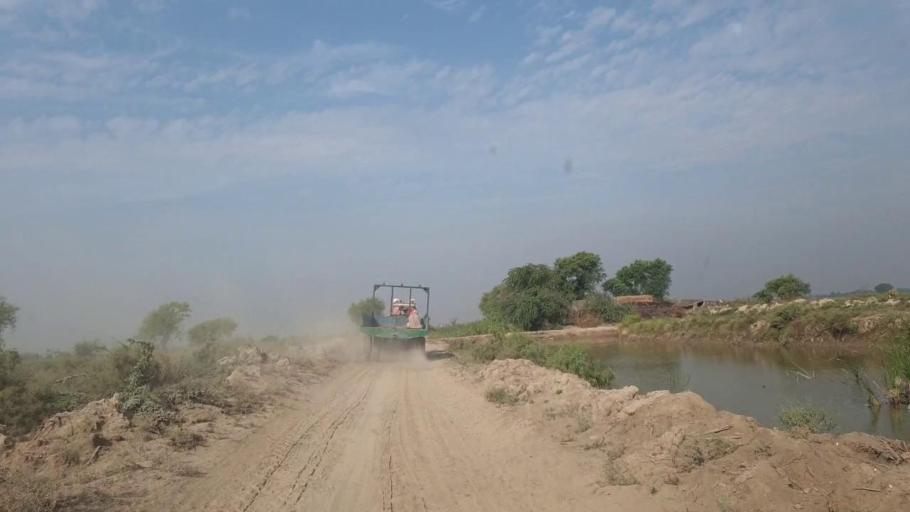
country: PK
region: Sindh
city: Tando Bago
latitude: 24.8744
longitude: 68.9604
